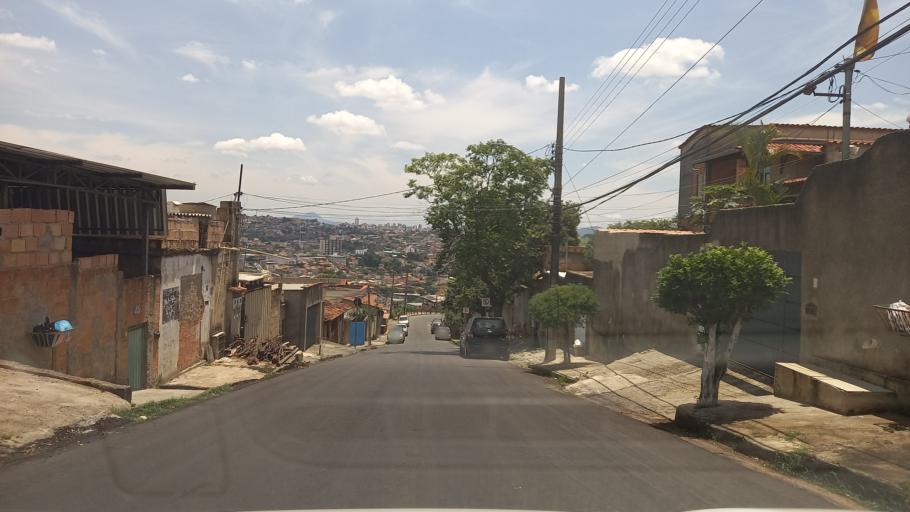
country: BR
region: Minas Gerais
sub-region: Contagem
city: Contagem
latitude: -19.9075
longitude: -44.0111
